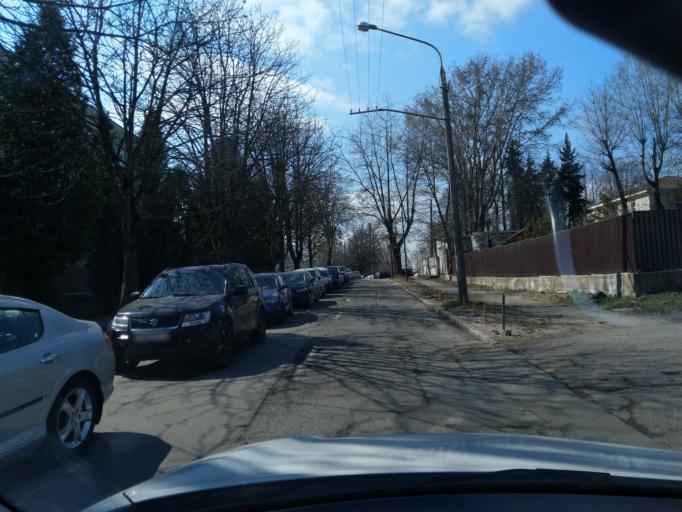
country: BY
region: Minsk
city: Syenitsa
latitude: 53.8704
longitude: 27.5068
